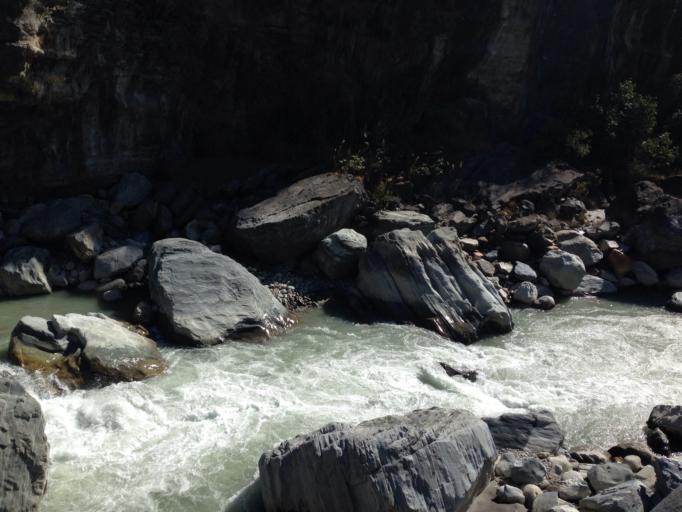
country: NP
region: Western Region
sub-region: Dhawalagiri Zone
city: Chitre
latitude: 28.4234
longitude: 83.5990
